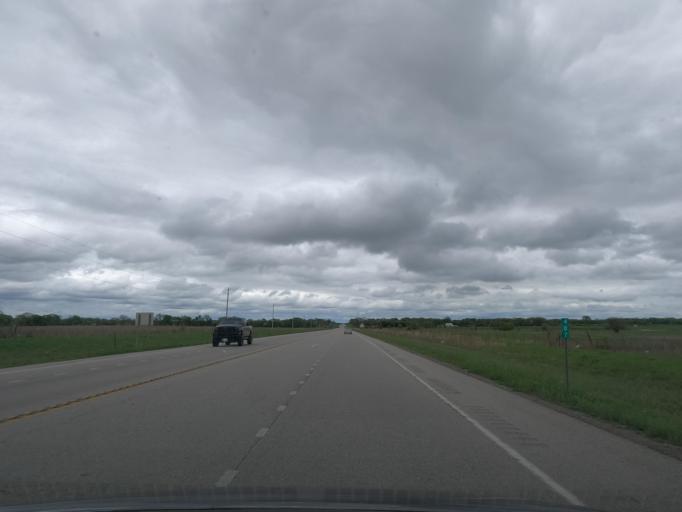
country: US
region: Kansas
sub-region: Labette County
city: Parsons
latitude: 37.3402
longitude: -95.1674
